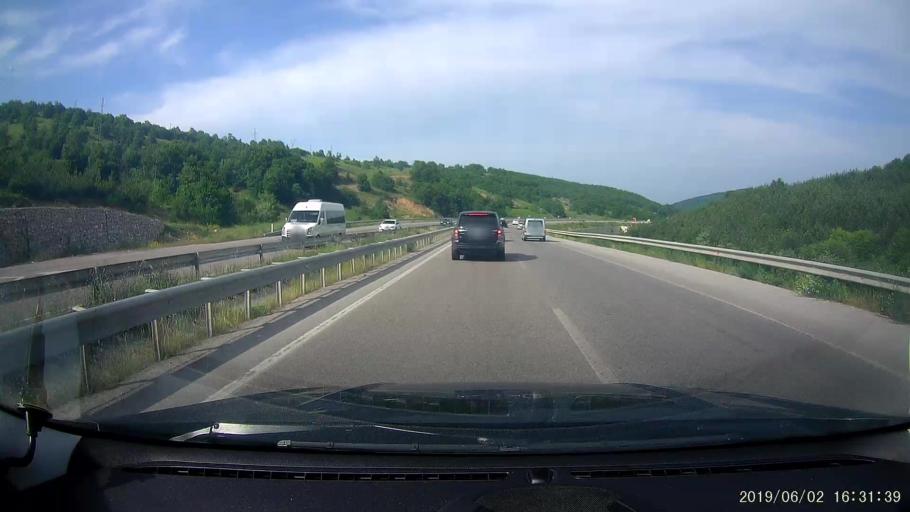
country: TR
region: Samsun
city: Ladik
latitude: 41.0342
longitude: 35.9042
